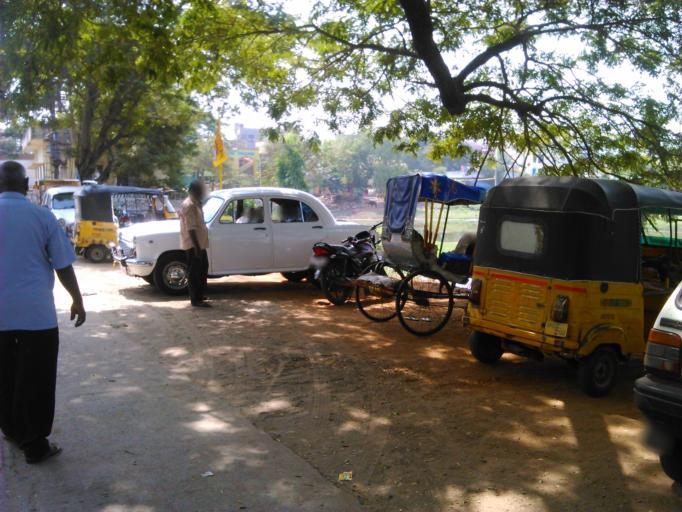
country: IN
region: Andhra Pradesh
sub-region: Guntur
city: Mangalagiri
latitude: 16.2420
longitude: 80.6496
